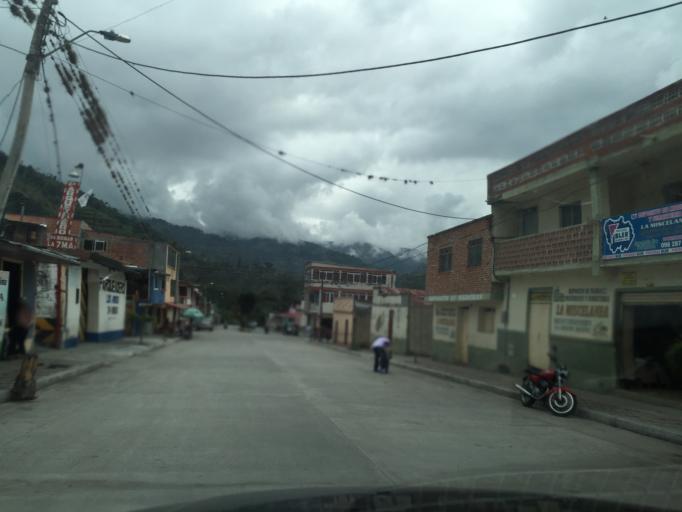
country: CO
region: Tolima
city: Cajamarca
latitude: 4.4402
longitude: -75.4272
